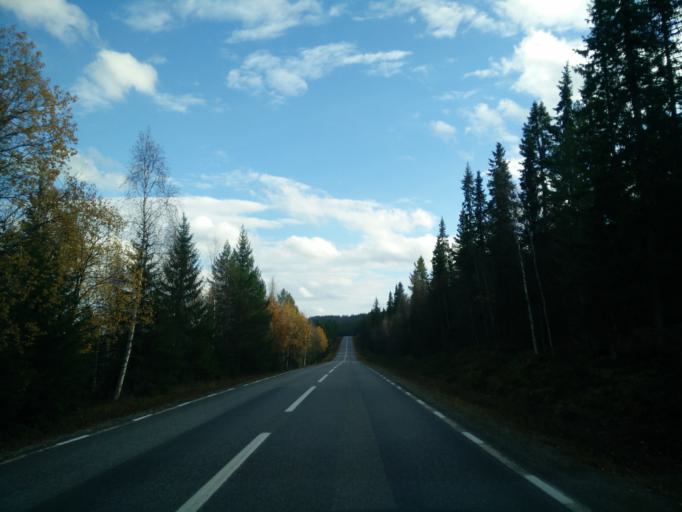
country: NO
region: Hedmark
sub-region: Engerdal
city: Engerdal
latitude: 62.4261
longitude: 12.7255
